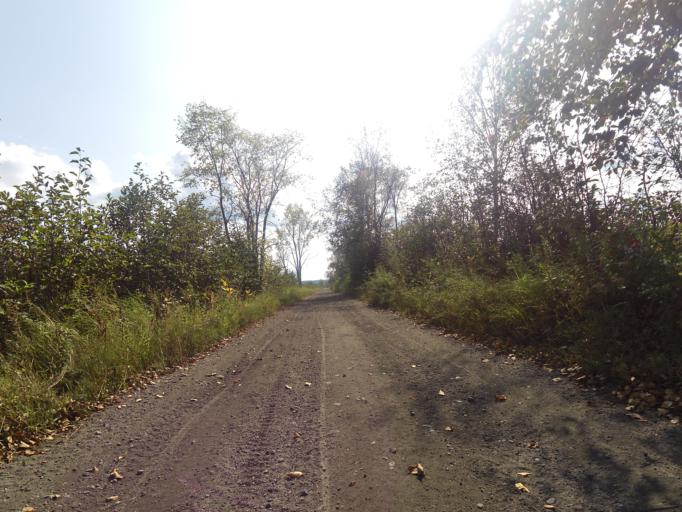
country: CA
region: Ontario
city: Renfrew
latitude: 45.1363
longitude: -76.6862
